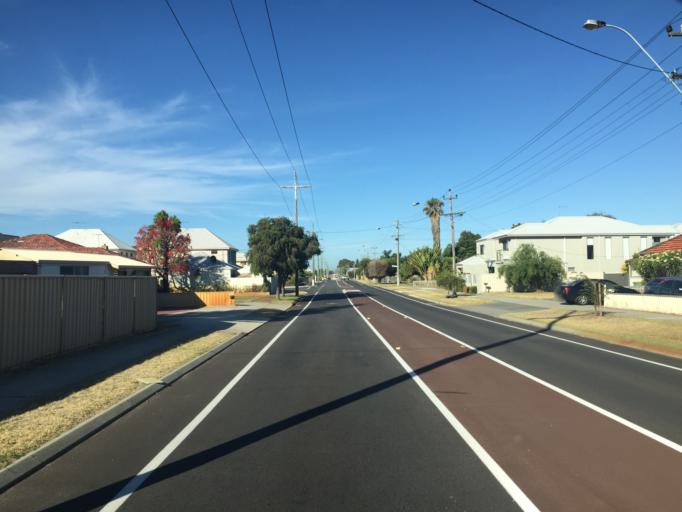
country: AU
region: Western Australia
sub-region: Belmont
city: Rivervale
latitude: -31.9639
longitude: 115.9249
